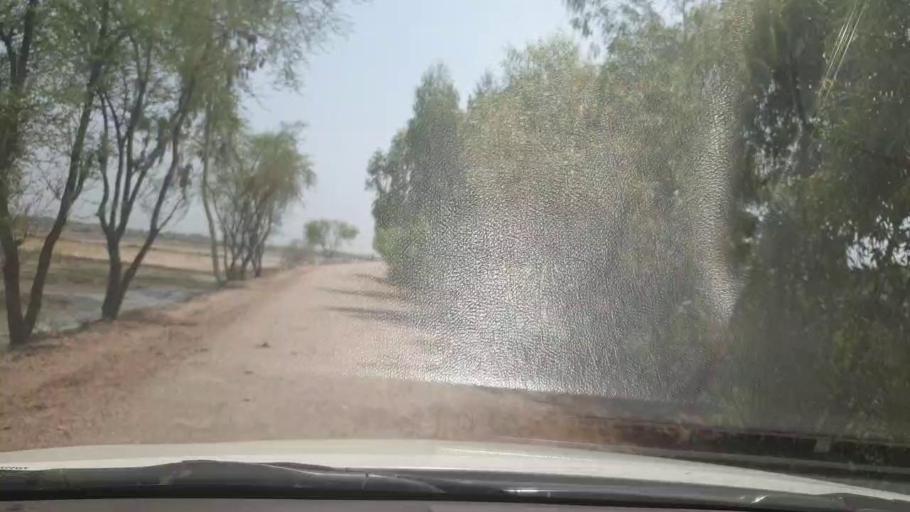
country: PK
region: Sindh
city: Shikarpur
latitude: 28.0388
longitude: 68.5736
